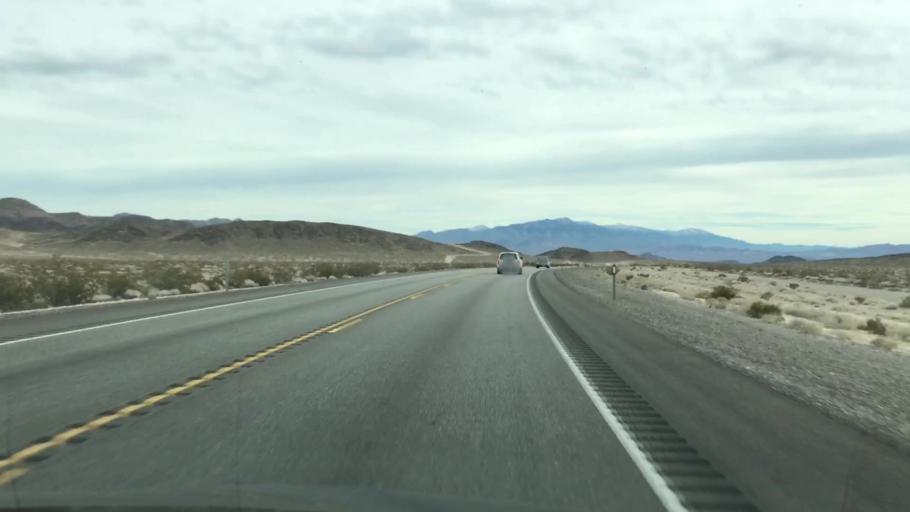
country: US
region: Nevada
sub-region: Nye County
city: Beatty
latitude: 36.6303
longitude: -116.3167
